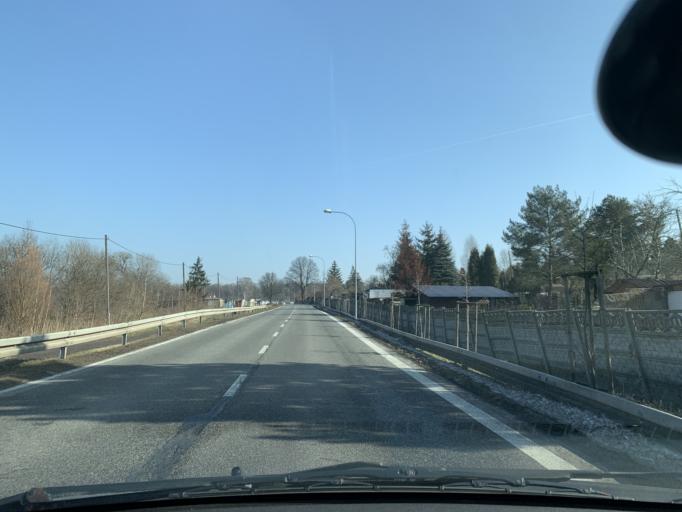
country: PL
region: Silesian Voivodeship
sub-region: Bytom
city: Bytom
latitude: 50.3601
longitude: 18.9158
